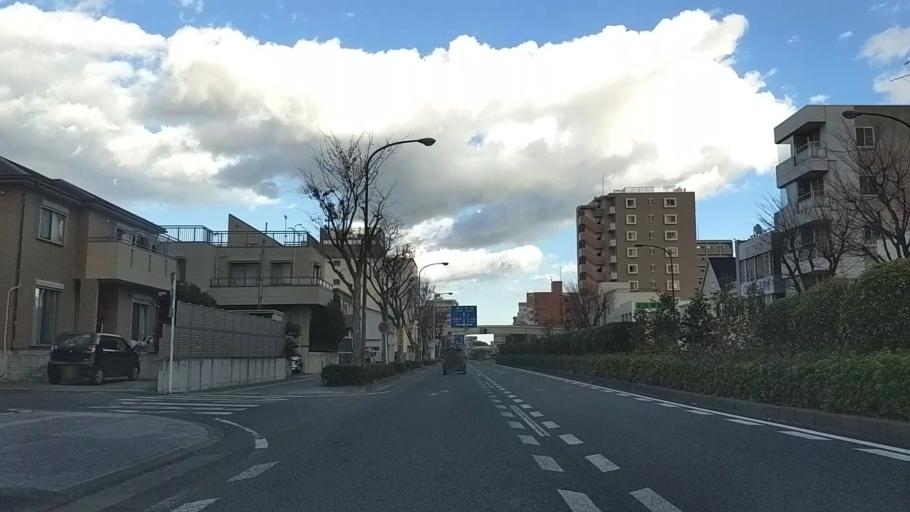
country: JP
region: Kanagawa
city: Hiratsuka
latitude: 35.3323
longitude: 139.3426
